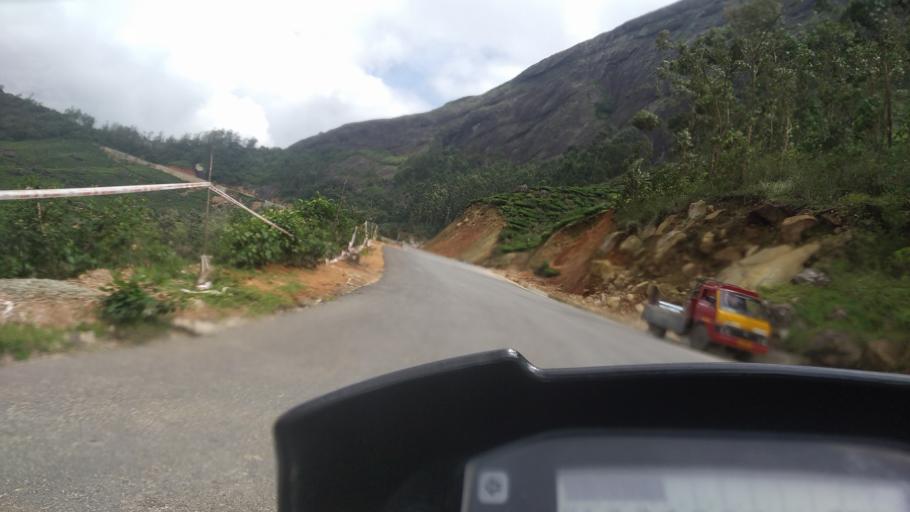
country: IN
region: Kerala
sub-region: Idukki
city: Munnar
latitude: 10.0394
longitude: 77.1130
